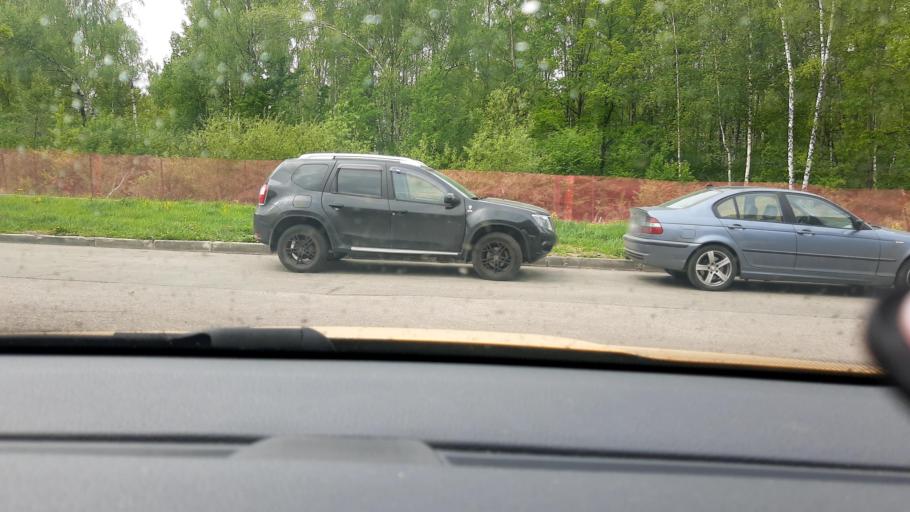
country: RU
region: Moscow
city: Khimki
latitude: 55.9233
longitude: 37.4408
